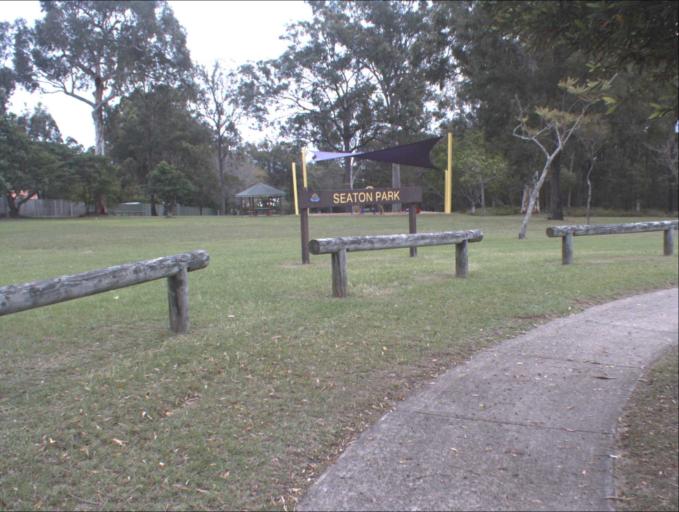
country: AU
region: Queensland
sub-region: Brisbane
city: Sunnybank Hills
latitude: -27.6628
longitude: 153.0211
